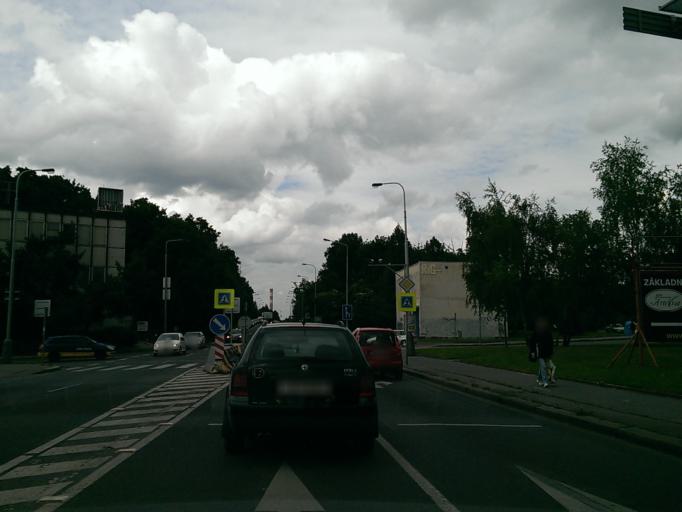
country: CZ
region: Praha
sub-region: Praha 4
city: Hodkovicky
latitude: 50.0242
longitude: 14.4420
